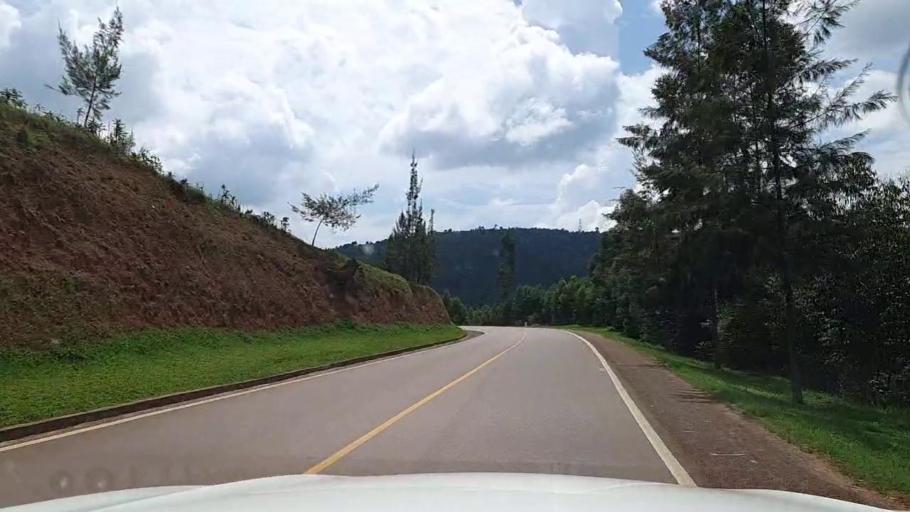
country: RW
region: Kigali
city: Kigali
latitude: -1.8157
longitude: 30.1090
